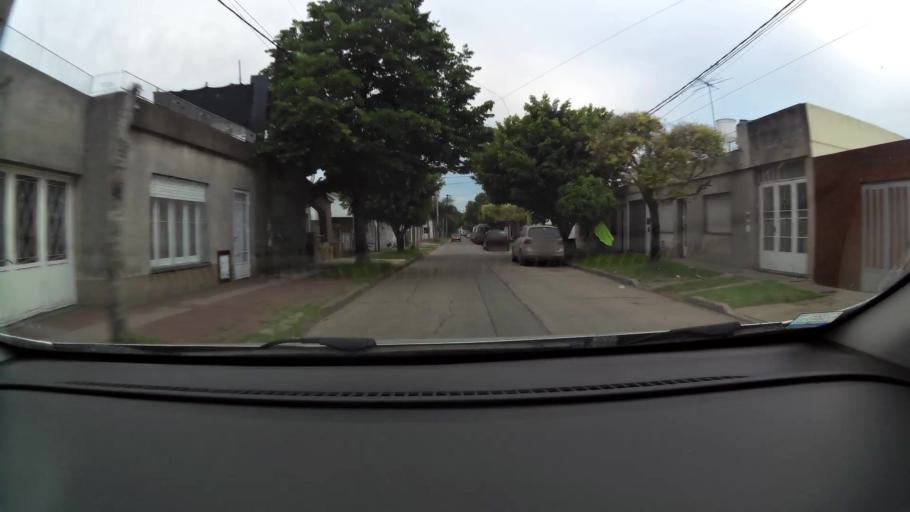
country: AR
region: Santa Fe
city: Granadero Baigorria
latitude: -32.8824
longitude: -60.6993
